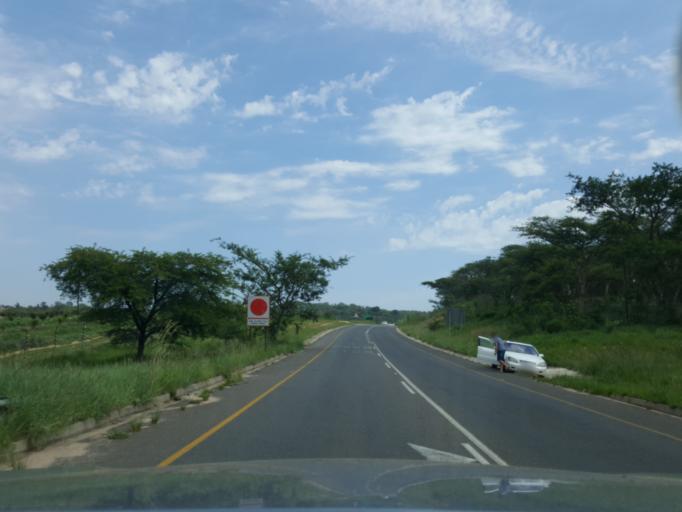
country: ZA
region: Mpumalanga
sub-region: Ehlanzeni District
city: White River
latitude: -25.3816
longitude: 31.0825
